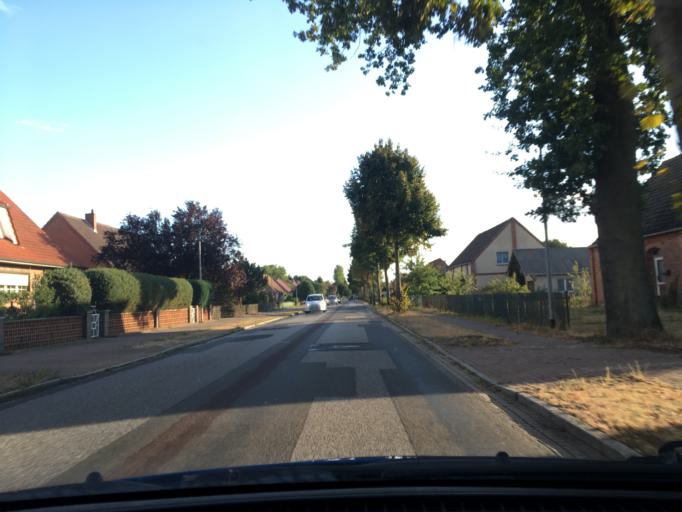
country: DE
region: Mecklenburg-Vorpommern
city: Neu Kaliss
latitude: 53.1856
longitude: 11.2965
